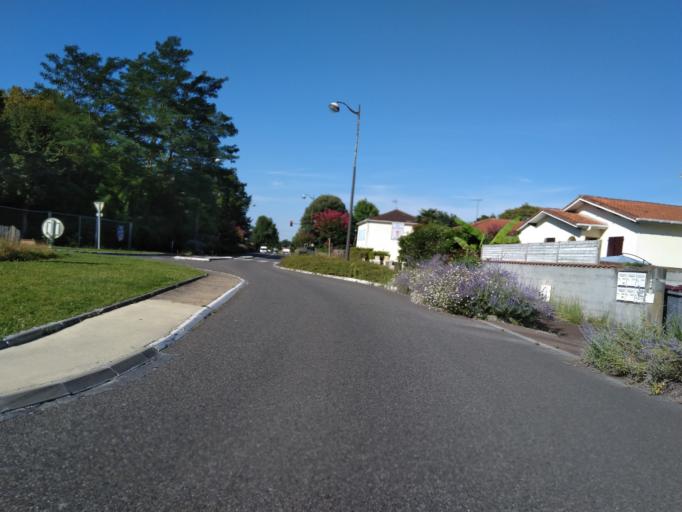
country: FR
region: Aquitaine
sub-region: Departement des Landes
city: Saint-Paul-les-Dax
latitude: 43.7275
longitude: -1.0430
